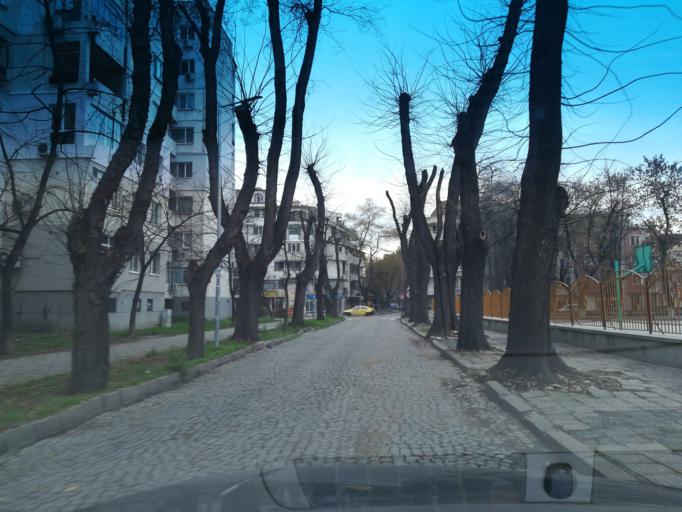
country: BG
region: Plovdiv
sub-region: Obshtina Plovdiv
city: Plovdiv
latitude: 42.1409
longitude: 24.7595
